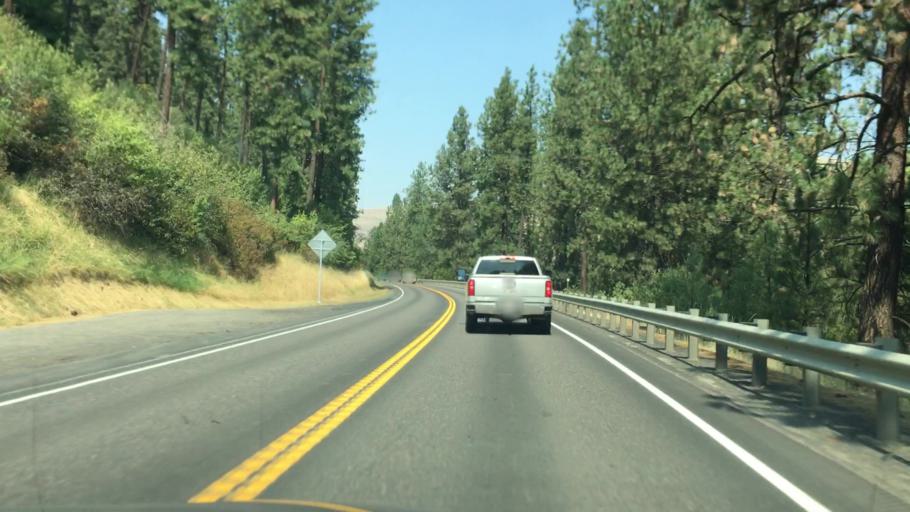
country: US
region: Idaho
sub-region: Nez Perce County
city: Lapwai
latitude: 46.5120
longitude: -116.5820
